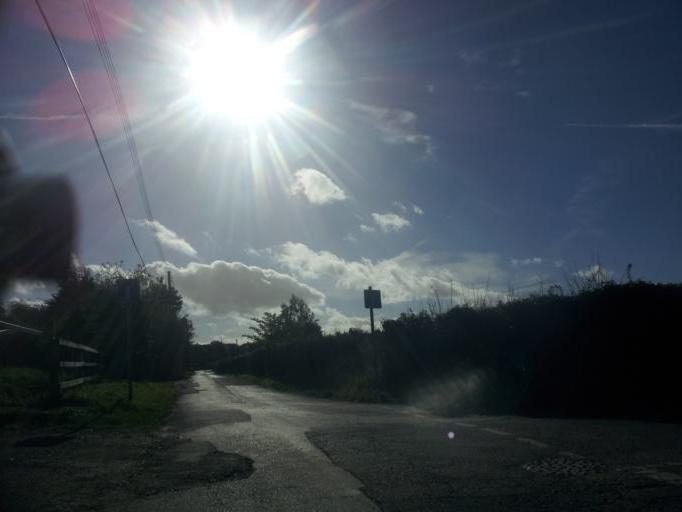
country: GB
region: England
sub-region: Kent
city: Rainham
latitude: 51.3826
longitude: 0.5904
